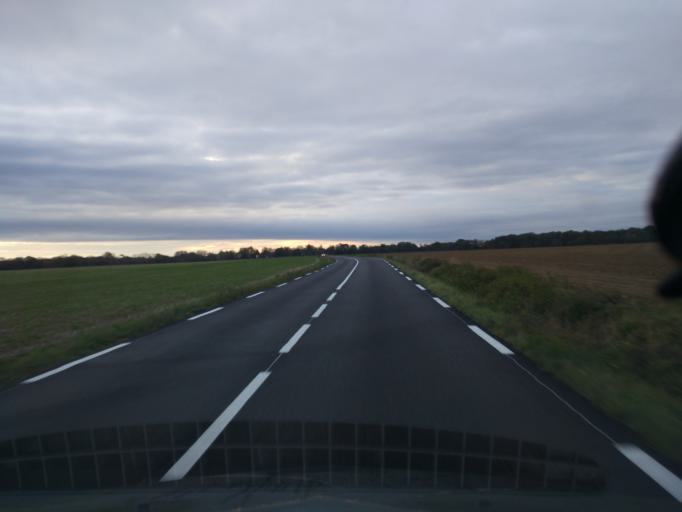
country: FR
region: Ile-de-France
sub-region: Departement de l'Essonne
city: Les Molieres
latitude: 48.6588
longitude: 2.0667
